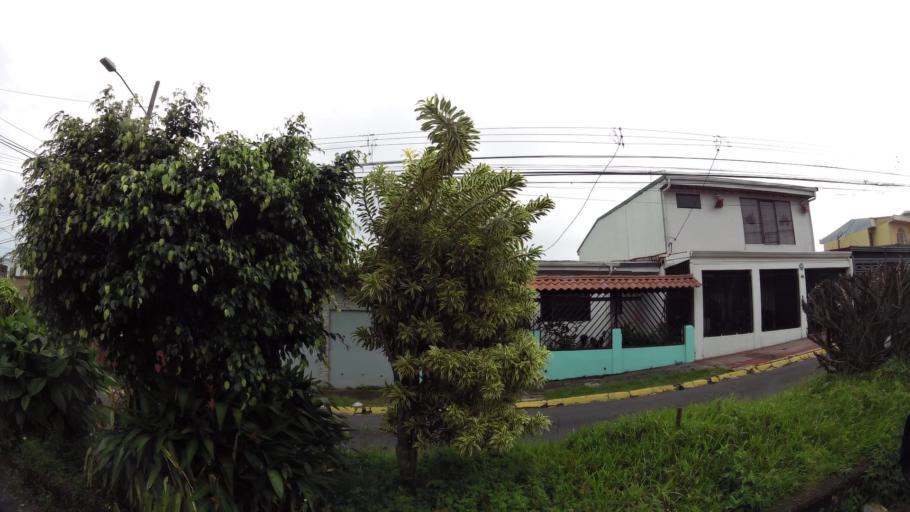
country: CR
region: San Jose
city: Purral
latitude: 9.9544
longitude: -84.0368
